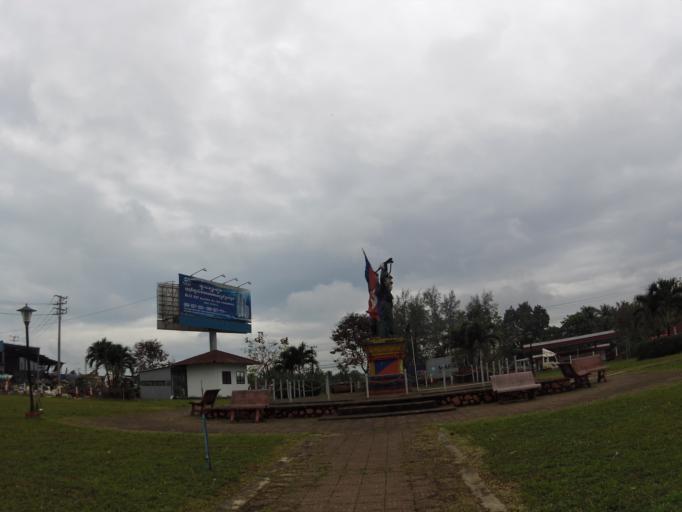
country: KH
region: Preah Sihanouk
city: Sihanoukville
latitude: 10.6349
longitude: 103.5342
